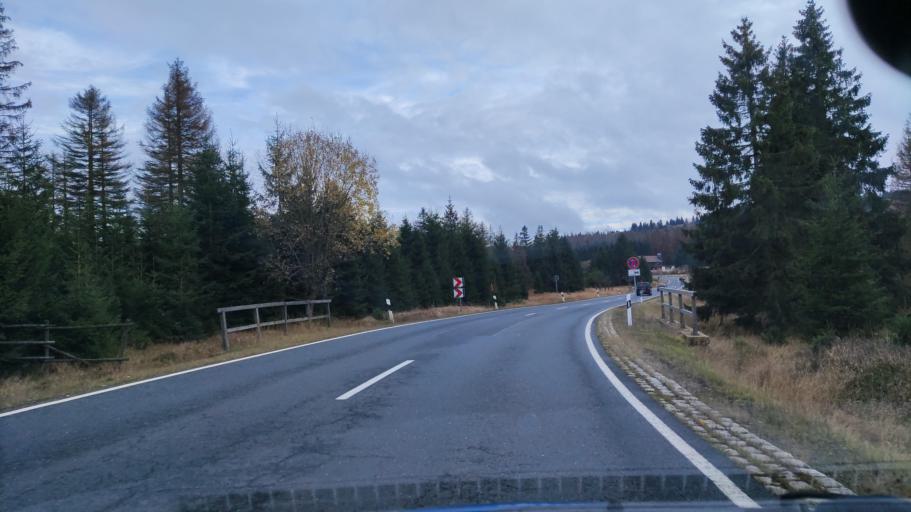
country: DE
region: Lower Saxony
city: Sankt Andreasberg
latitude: 51.7638
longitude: 10.5102
